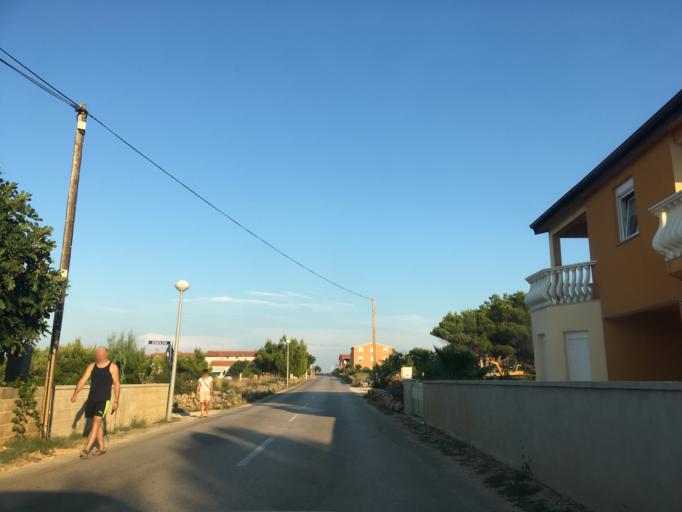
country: HR
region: Zadarska
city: Vir
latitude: 44.3002
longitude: 15.1112
